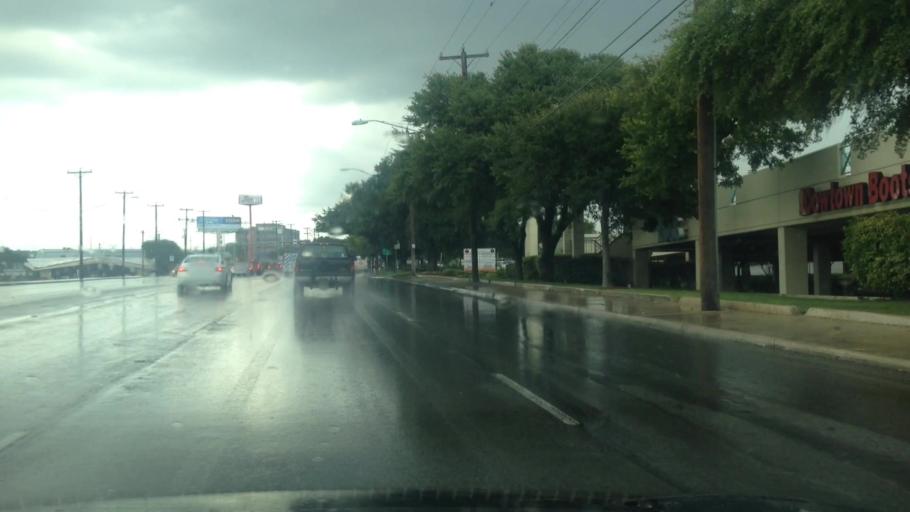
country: US
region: Texas
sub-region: Bexar County
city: Balcones Heights
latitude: 29.4908
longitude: -98.5520
